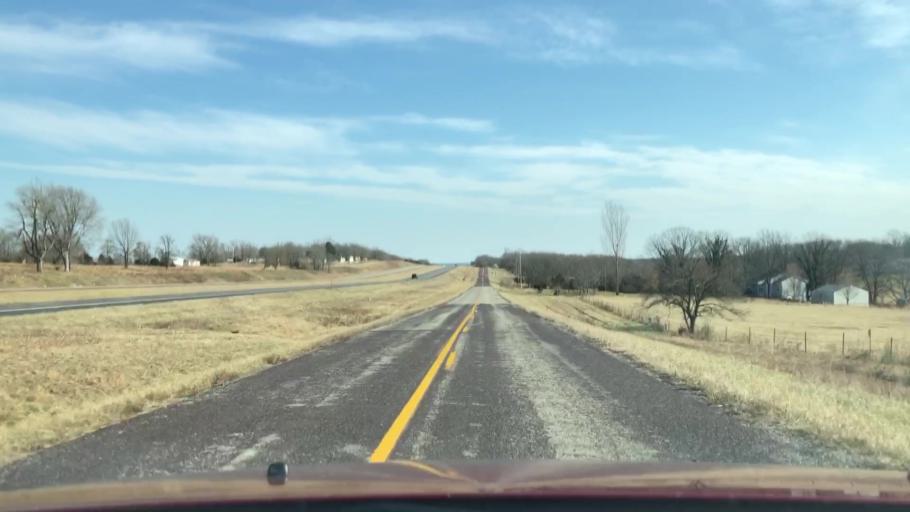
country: US
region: Missouri
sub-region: Wright County
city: Mansfield
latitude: 37.1116
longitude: -92.6349
